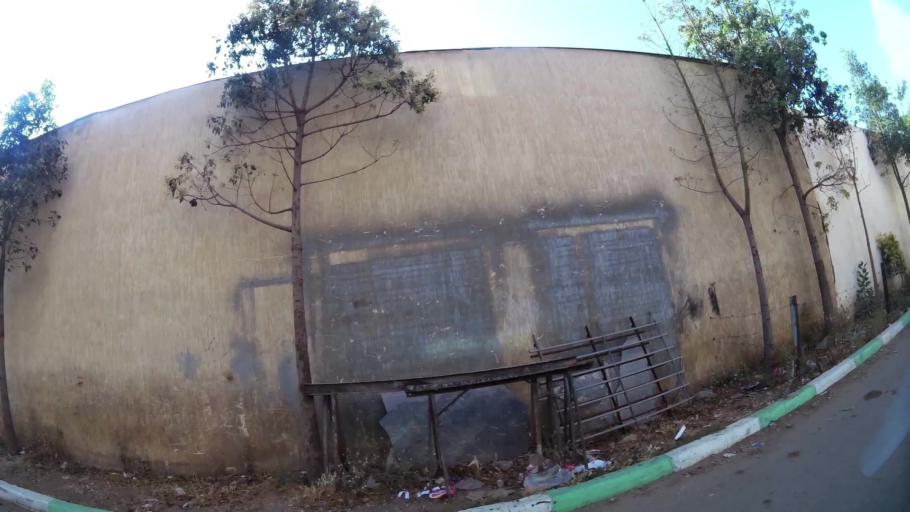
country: MA
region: Rabat-Sale-Zemmour-Zaer
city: Sale
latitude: 34.0596
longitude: -6.7898
